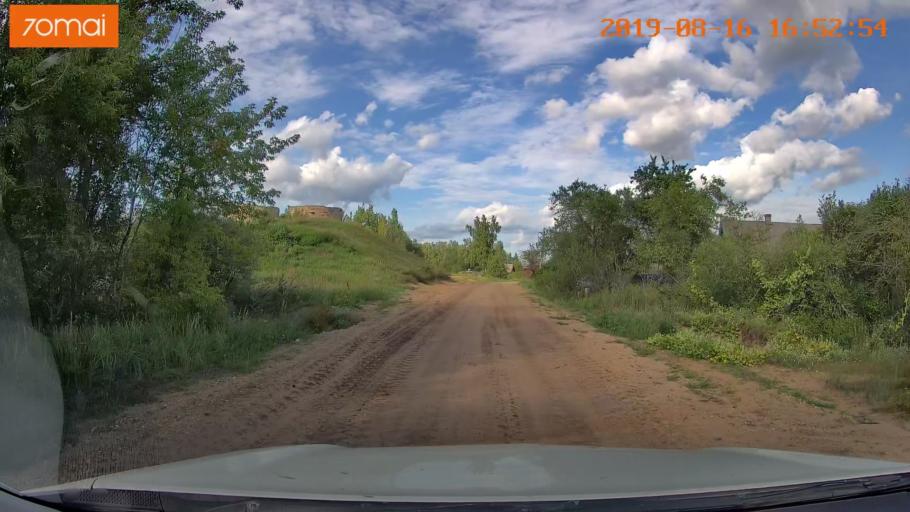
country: BY
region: Mogilev
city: Asipovichy
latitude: 53.2538
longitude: 28.8057
